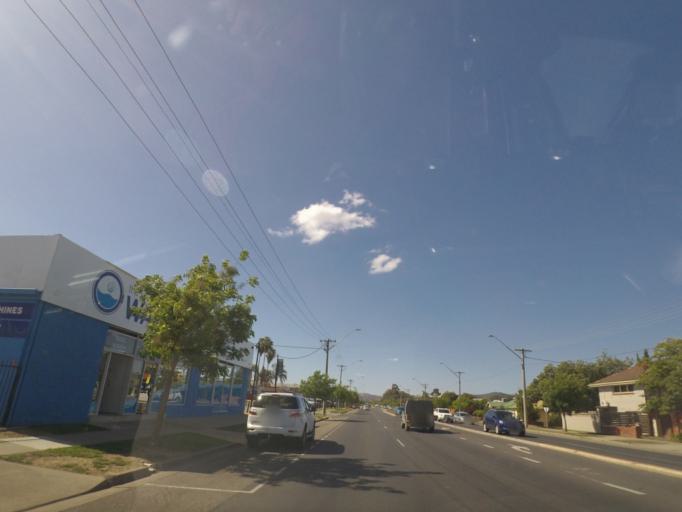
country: AU
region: New South Wales
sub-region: Albury Municipality
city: Albury
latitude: -36.0680
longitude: 146.9305
